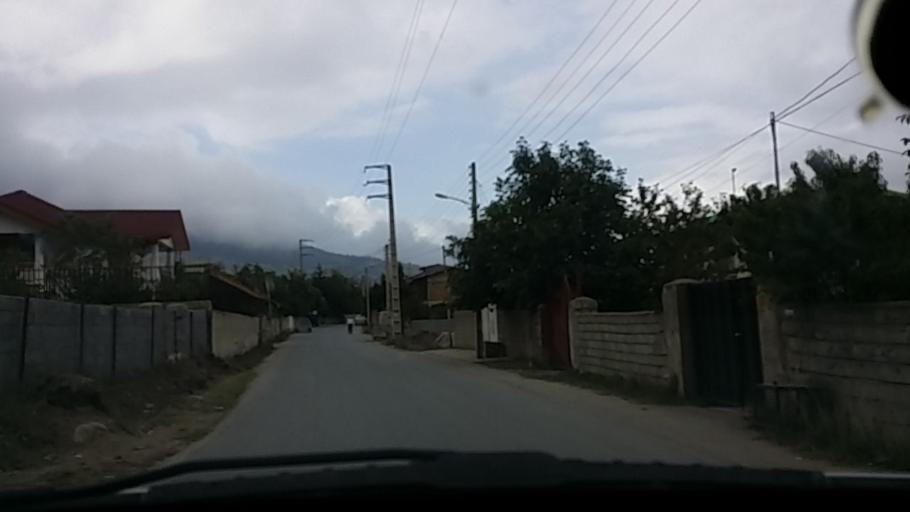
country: IR
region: Mazandaran
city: `Abbasabad
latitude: 36.5110
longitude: 51.1715
